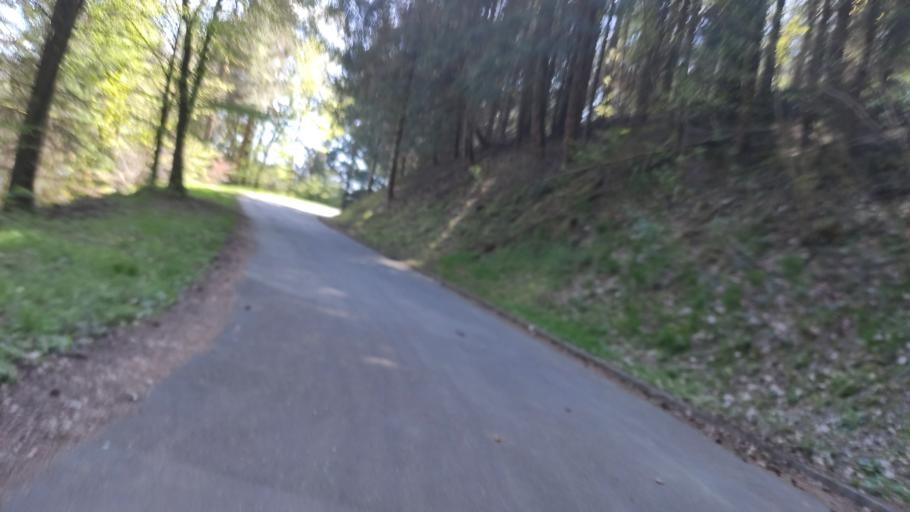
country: DE
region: Bavaria
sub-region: Upper Franconia
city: Steinwiesen
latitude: 50.3286
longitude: 11.4870
